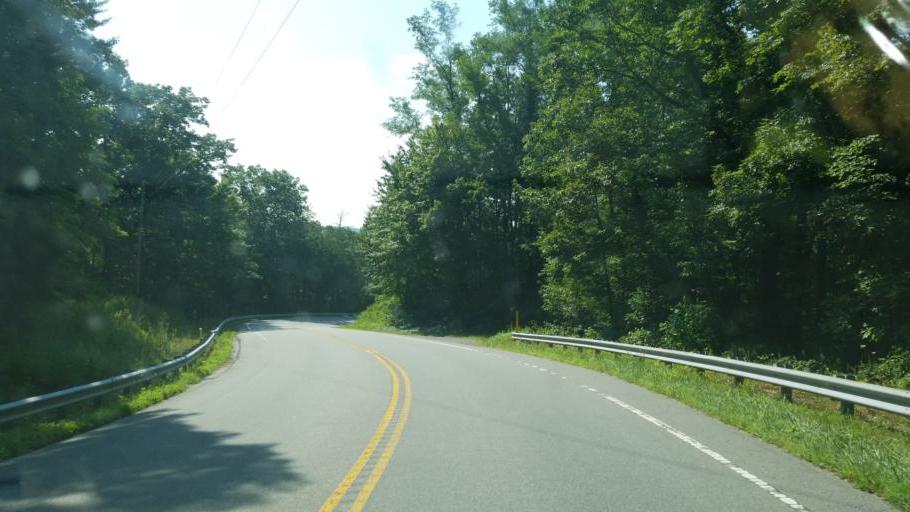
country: US
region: North Carolina
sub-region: Burke County
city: Glen Alpine
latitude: 35.9228
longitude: -81.8149
